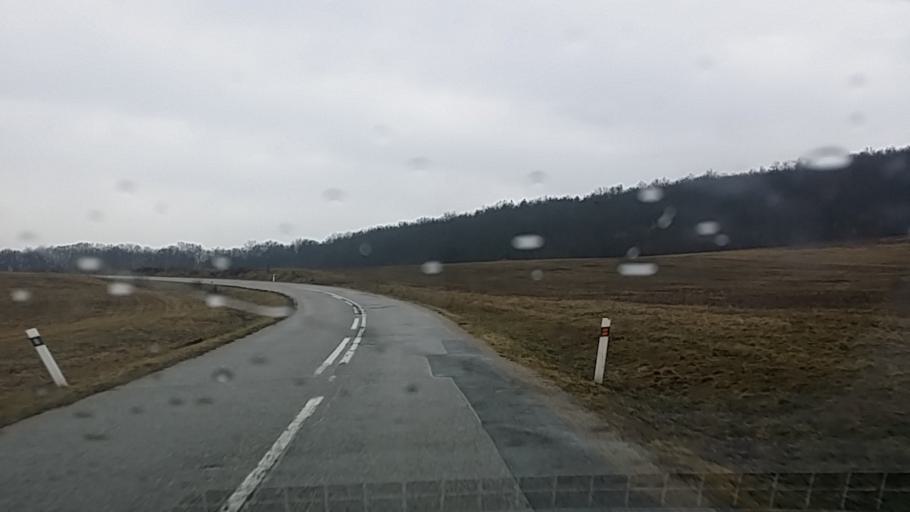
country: HU
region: Borsod-Abauj-Zemplen
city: Rudabanya
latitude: 48.4751
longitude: 20.4831
